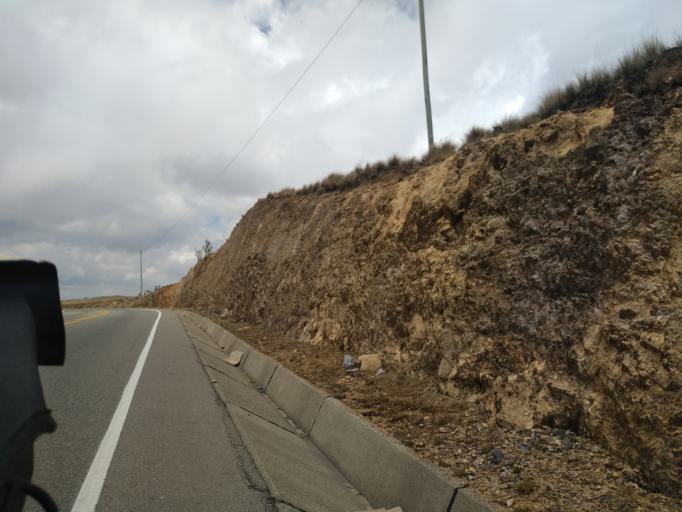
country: PE
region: La Libertad
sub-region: Provincia de Santiago de Chuco
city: Quiruvilca
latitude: -7.9562
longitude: -78.1955
